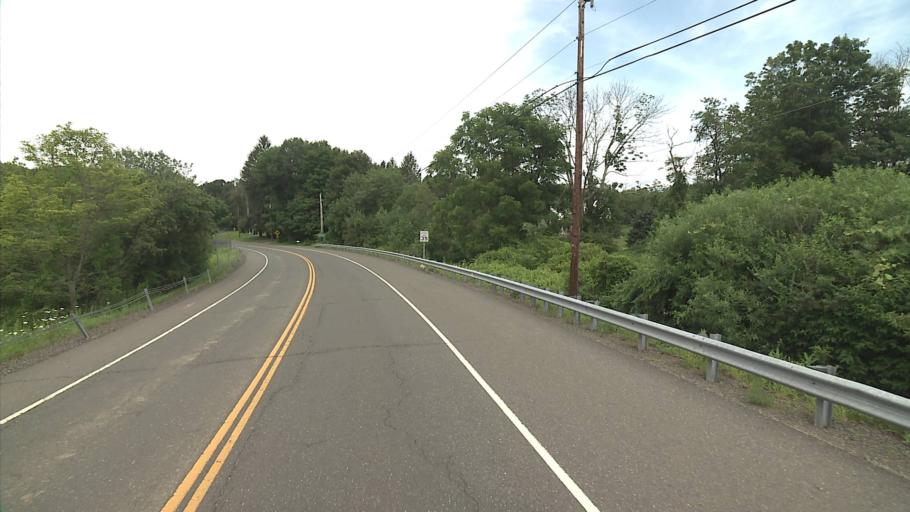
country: US
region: Connecticut
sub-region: Litchfield County
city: New Milford
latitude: 41.5676
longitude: -73.3160
